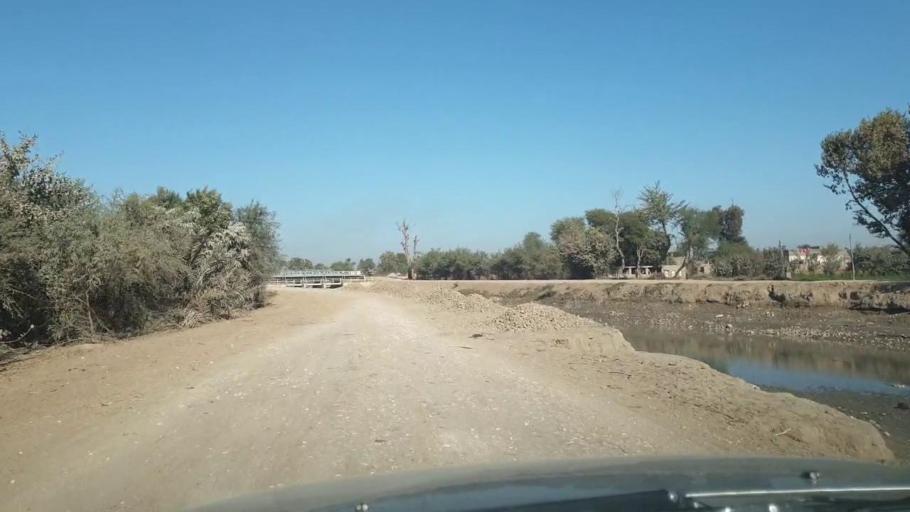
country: PK
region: Sindh
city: Ghotki
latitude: 28.0710
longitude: 69.3485
